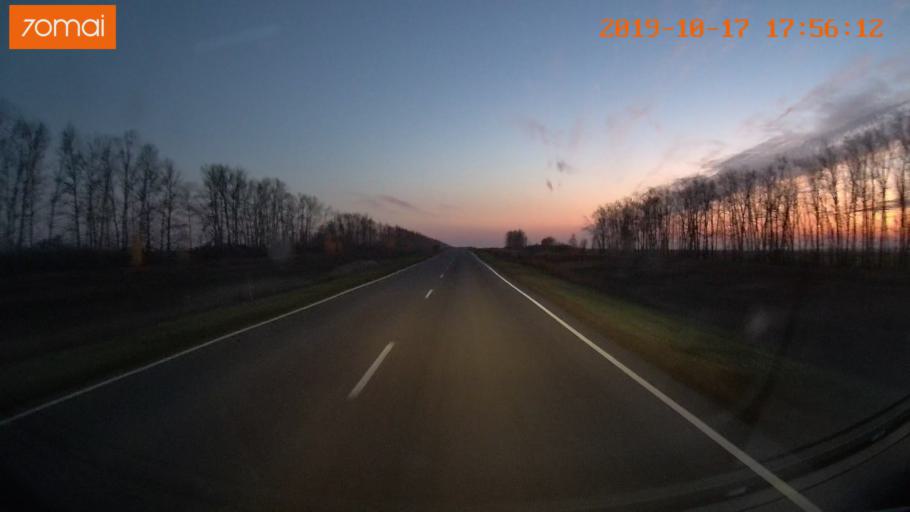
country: RU
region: Tula
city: Kurkino
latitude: 53.5828
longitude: 38.6495
